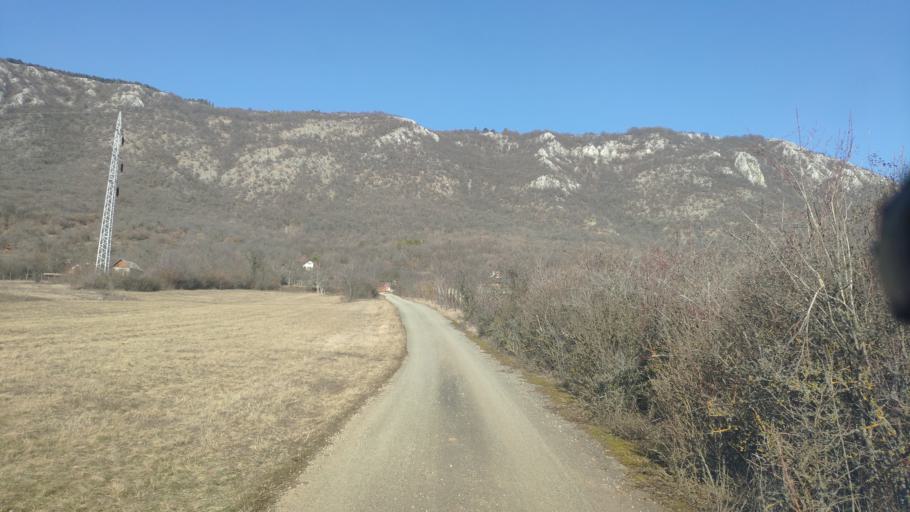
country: SK
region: Kosicky
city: Roznava
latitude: 48.5995
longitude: 20.7216
